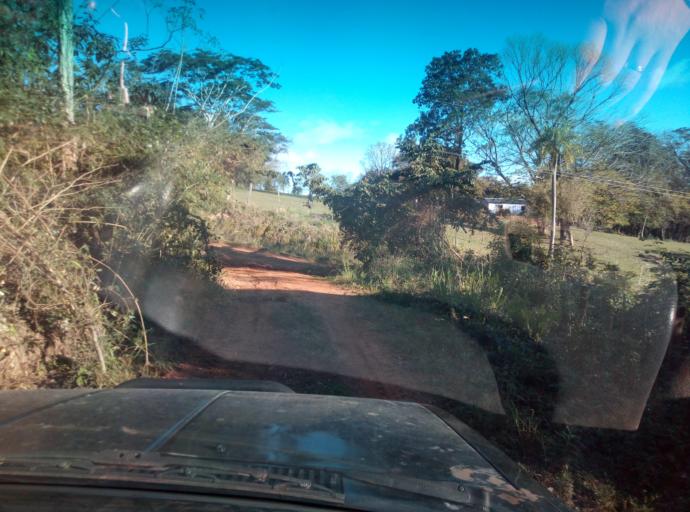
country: PY
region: Caaguazu
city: Carayao
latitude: -25.1896
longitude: -56.2628
